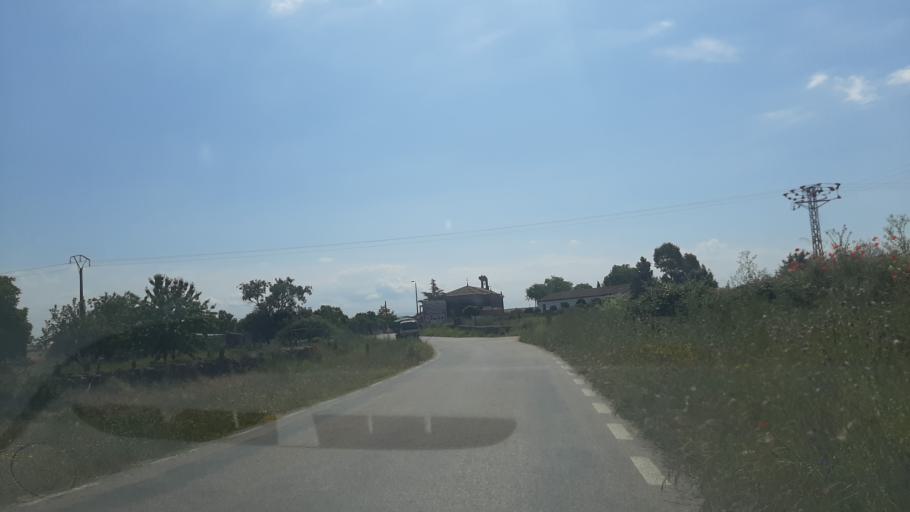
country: ES
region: Castille and Leon
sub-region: Provincia de Salamanca
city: Gallegos de Arganan
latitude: 40.6327
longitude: -6.7079
